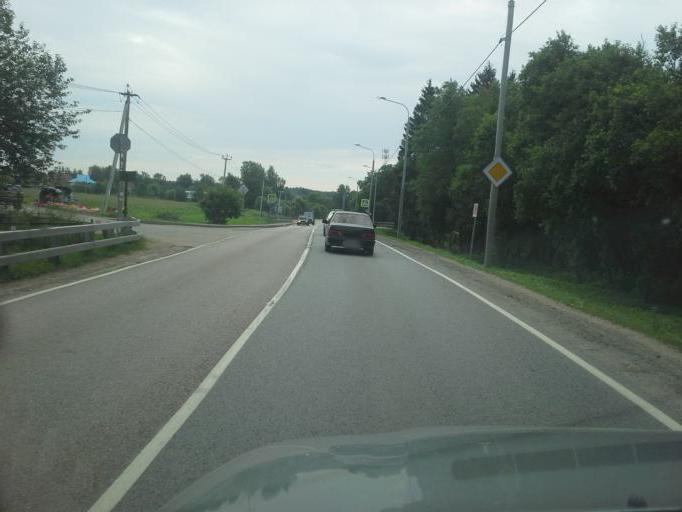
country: RU
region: Moskovskaya
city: Kokoshkino
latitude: 55.5714
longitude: 37.1423
